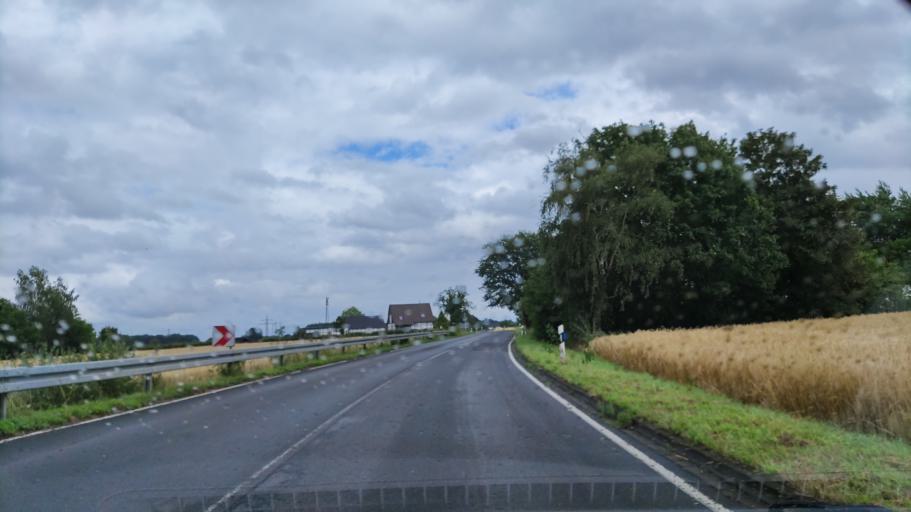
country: DE
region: North Rhine-Westphalia
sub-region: Regierungsbezirk Arnsberg
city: Welver
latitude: 51.6623
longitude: 7.9127
